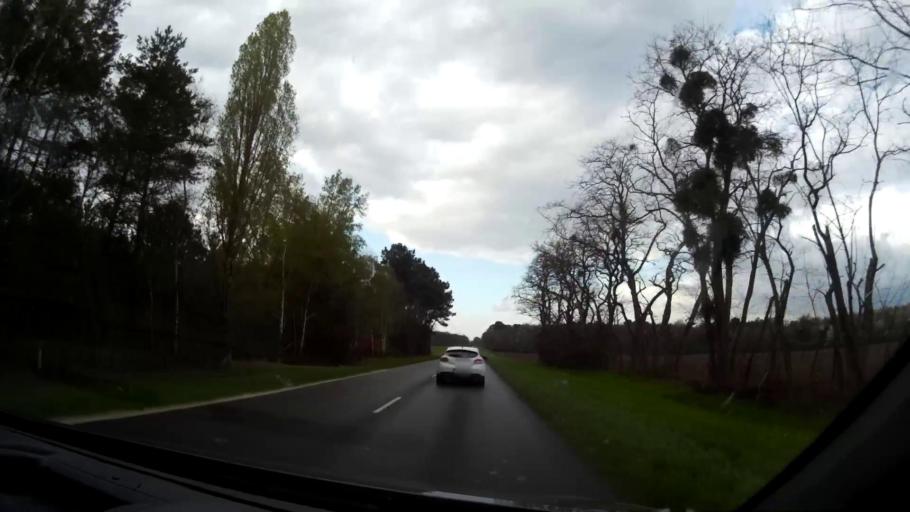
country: FR
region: Centre
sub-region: Departement du Loir-et-Cher
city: Contres
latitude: 47.4570
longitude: 1.4255
